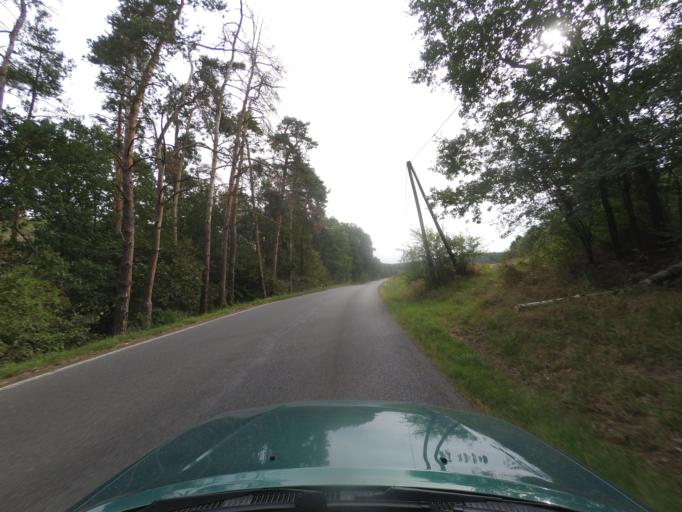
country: CZ
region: Plzensky
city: Hostoun
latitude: 49.5632
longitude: 12.8208
